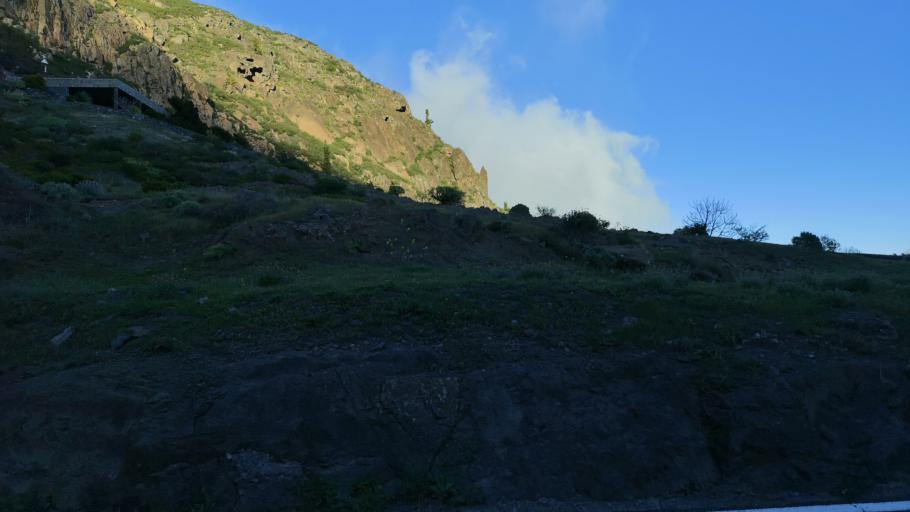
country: ES
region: Canary Islands
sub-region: Provincia de Santa Cruz de Tenerife
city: Alajero
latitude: 28.0863
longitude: -17.2499
